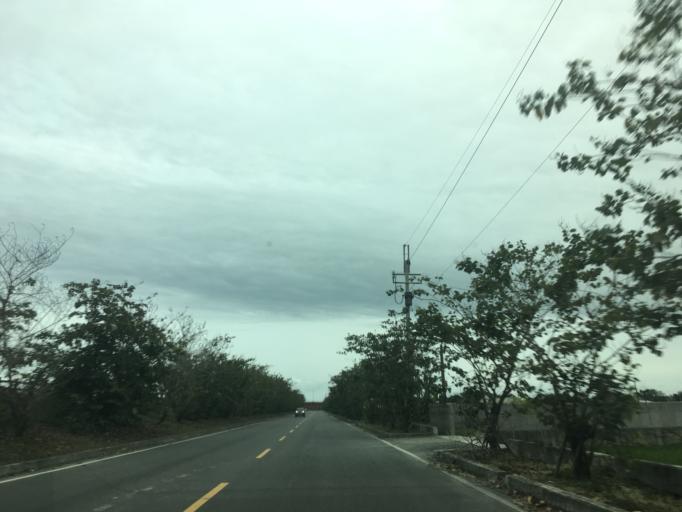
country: TW
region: Taiwan
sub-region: Taitung
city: Taitung
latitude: 22.7949
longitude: 121.1378
